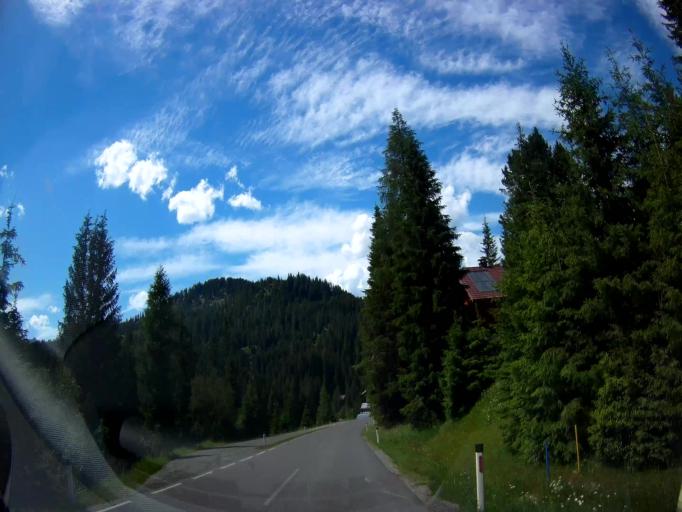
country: AT
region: Carinthia
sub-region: Politischer Bezirk Sankt Veit an der Glan
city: Glodnitz
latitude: 46.9483
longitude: 14.0260
